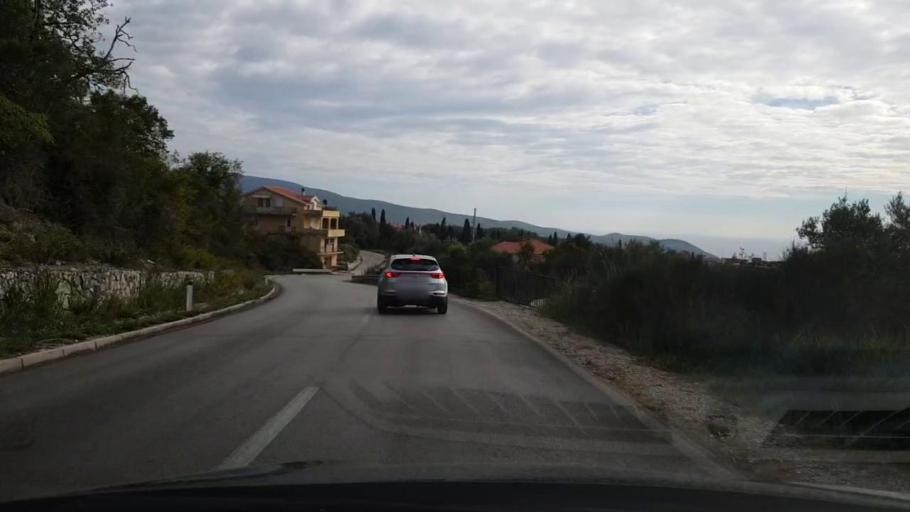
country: ME
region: Herceg Novi
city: Herceg-Novi
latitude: 42.4651
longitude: 18.5450
